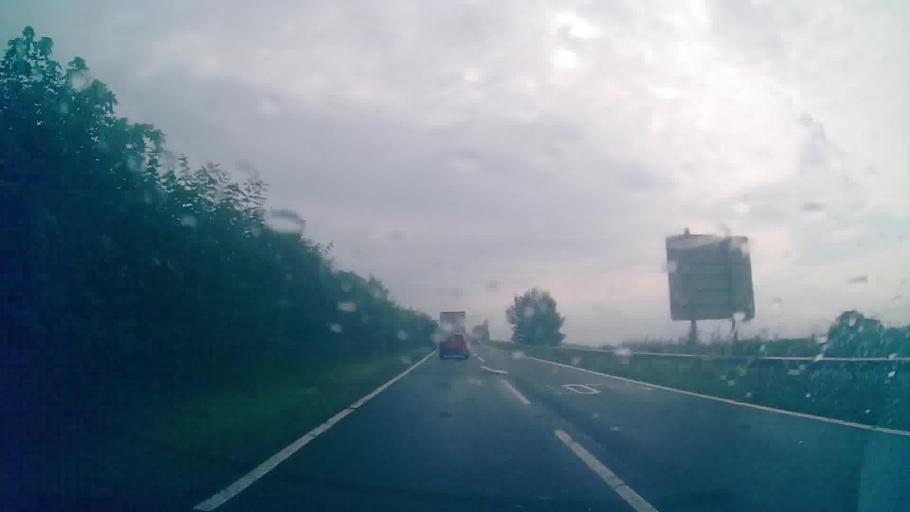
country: GB
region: Scotland
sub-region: Dumfries and Galloway
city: Lochmaben
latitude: 55.0580
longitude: -3.4743
